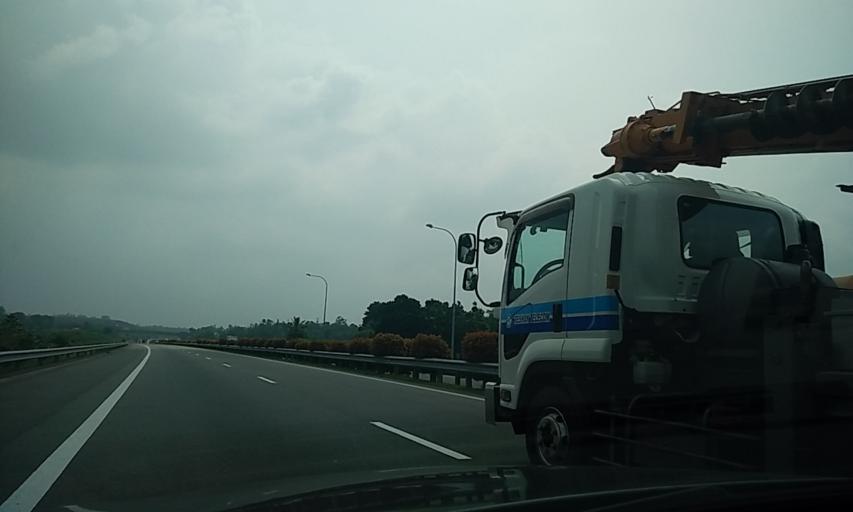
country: LK
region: Western
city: Homagama
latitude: 6.8796
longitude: 79.9770
